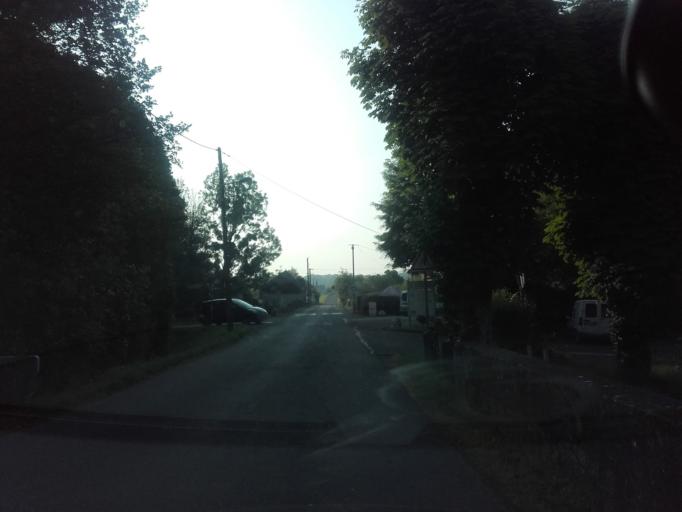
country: FR
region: Centre
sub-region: Departement d'Indre-et-Loire
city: Reugny
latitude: 47.4517
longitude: 0.8741
